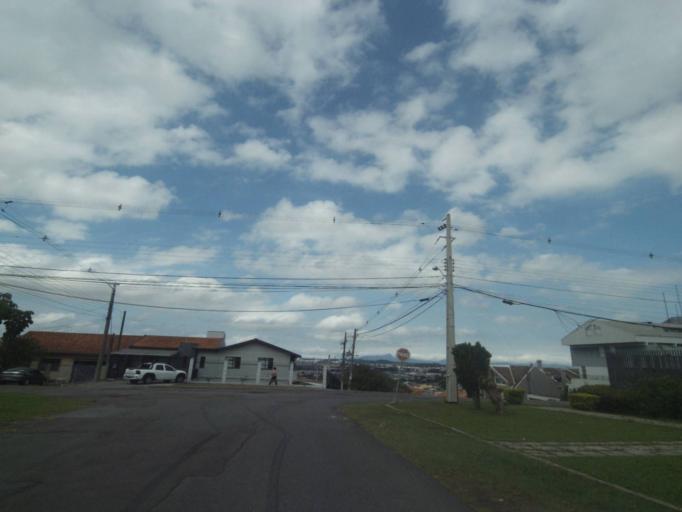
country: BR
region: Parana
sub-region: Pinhais
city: Pinhais
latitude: -25.4146
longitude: -49.2082
